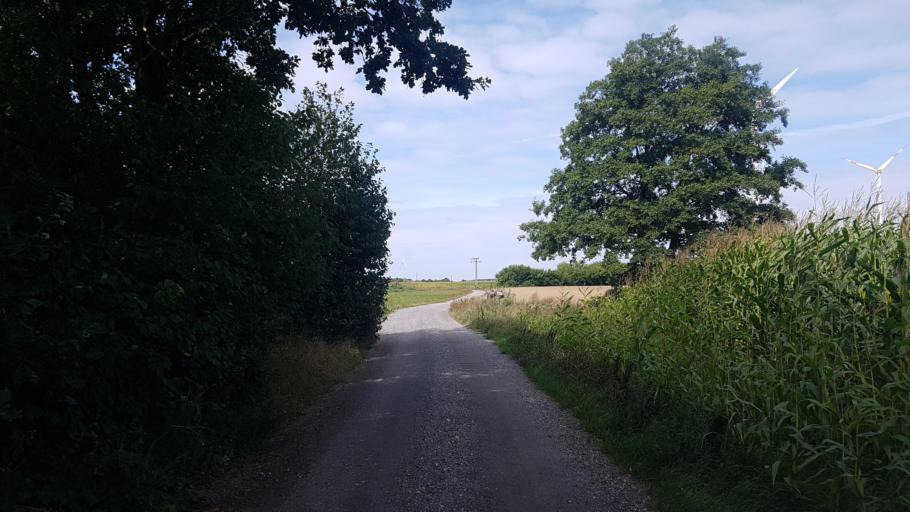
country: DE
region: Brandenburg
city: Bronkow
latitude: 51.6404
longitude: 13.8796
